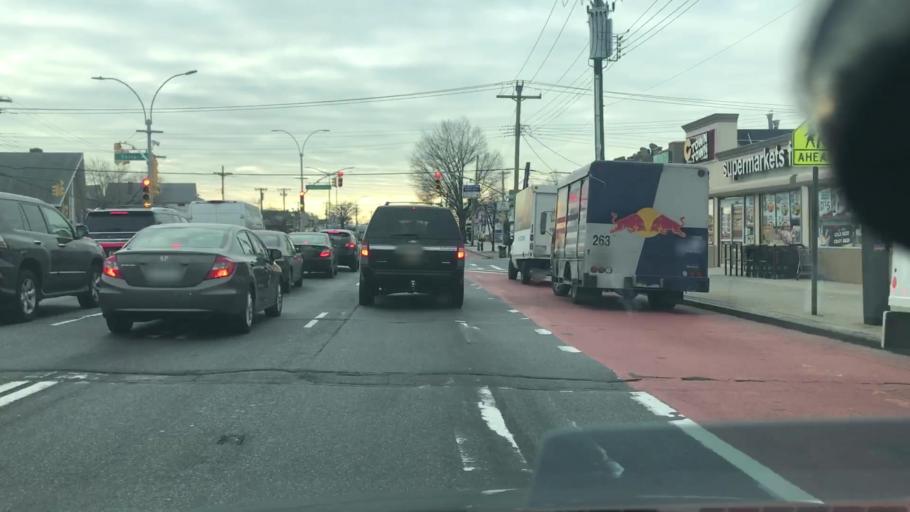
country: US
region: New York
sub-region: Queens County
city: Borough of Queens
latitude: 40.6773
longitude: -73.8440
